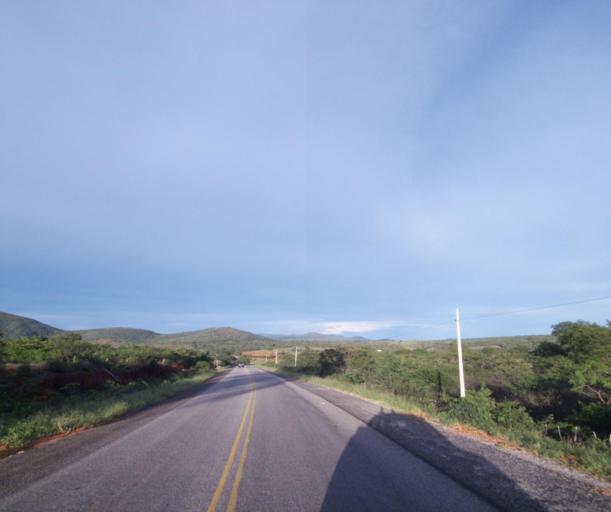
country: BR
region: Bahia
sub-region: Cacule
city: Cacule
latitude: -14.2084
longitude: -42.0855
